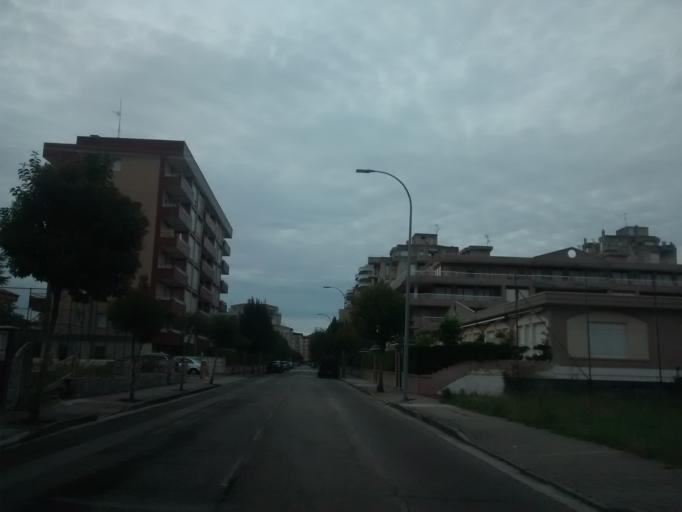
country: ES
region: Cantabria
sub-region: Provincia de Cantabria
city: Colindres
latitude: 43.4172
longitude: -3.4415
